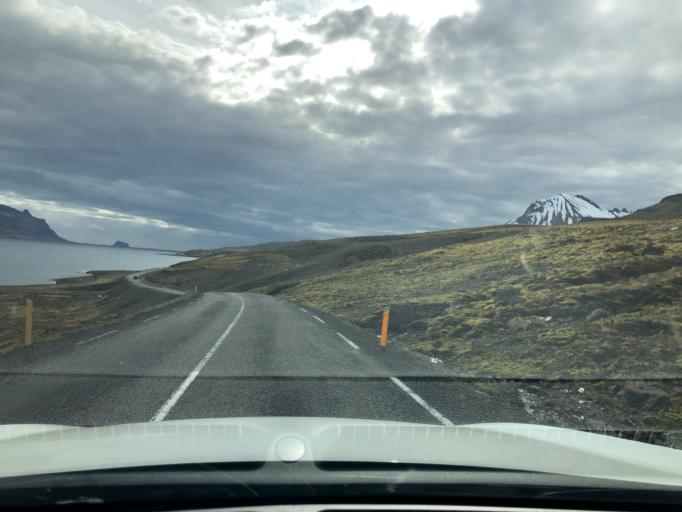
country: IS
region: East
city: Eskifjoerdur
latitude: 64.9069
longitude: -13.9720
